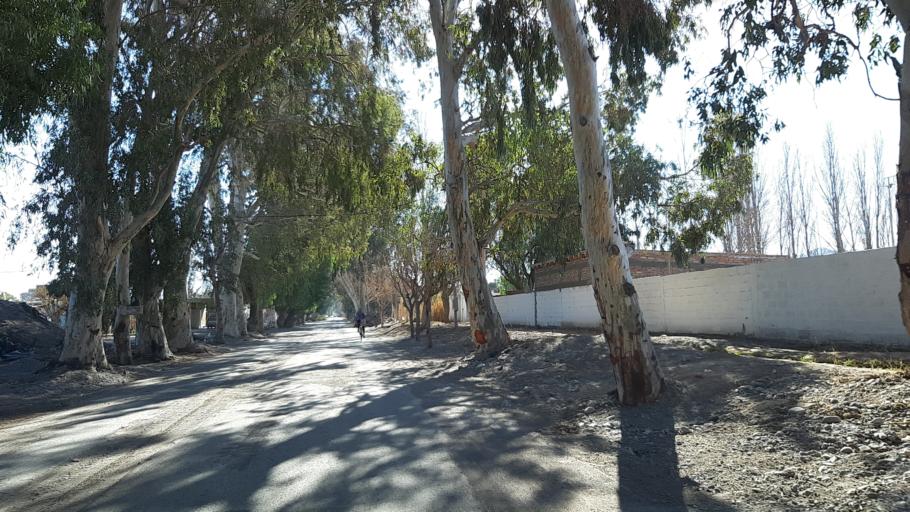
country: AR
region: San Juan
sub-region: Departamento de Zonda
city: Zonda
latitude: -31.5513
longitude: -68.7278
